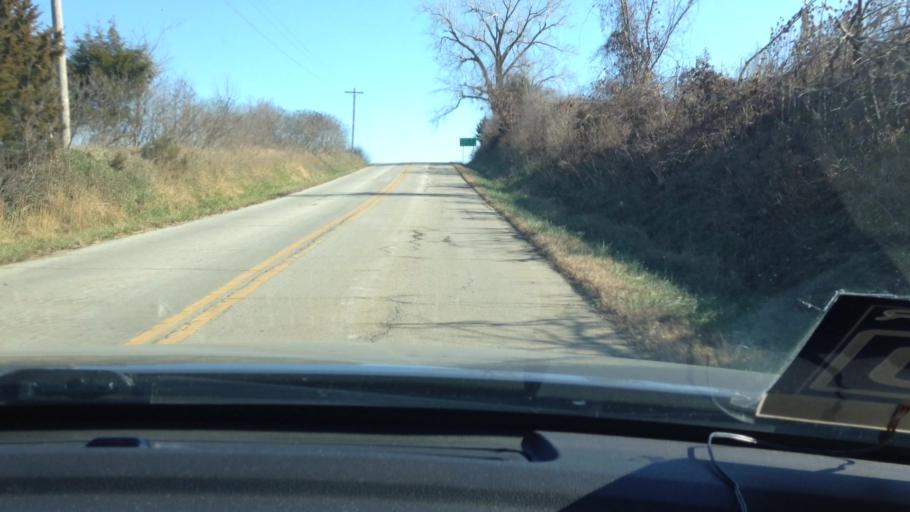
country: US
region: Missouri
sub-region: Platte County
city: Weston
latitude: 39.4977
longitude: -94.8482
